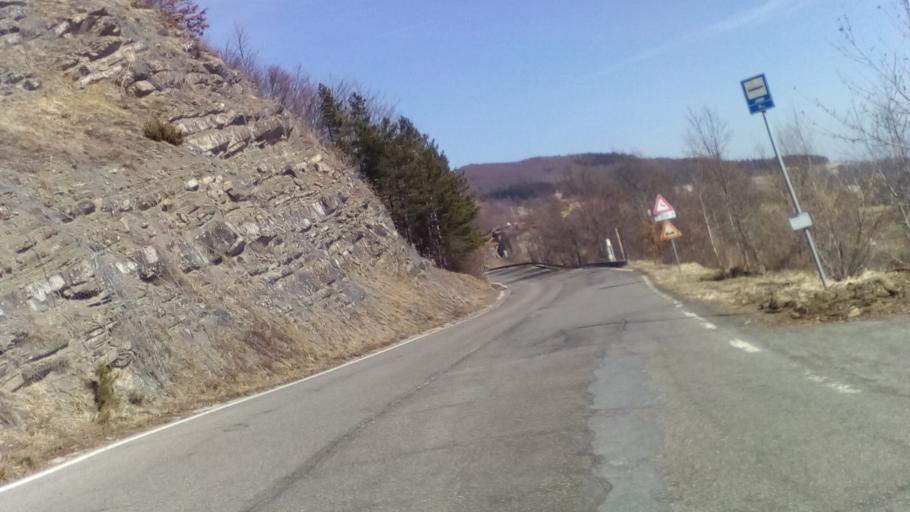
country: IT
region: Emilia-Romagna
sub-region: Provincia di Modena
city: Riolunato
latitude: 44.2622
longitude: 10.6637
